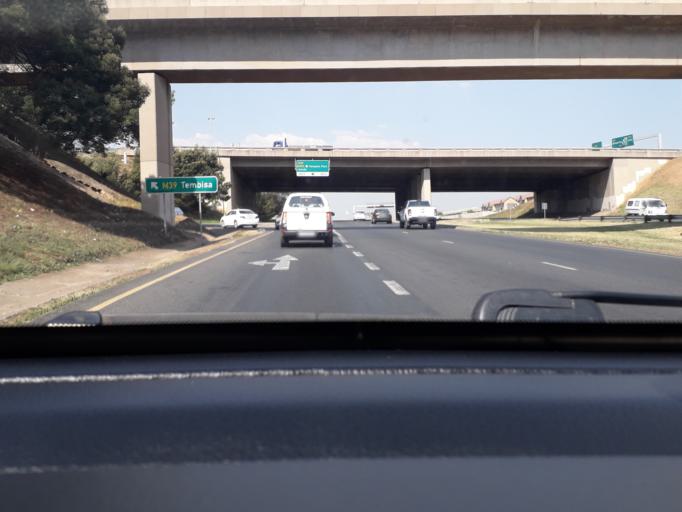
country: ZA
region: Gauteng
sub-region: City of Johannesburg Metropolitan Municipality
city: Modderfontein
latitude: -26.0894
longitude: 28.1898
